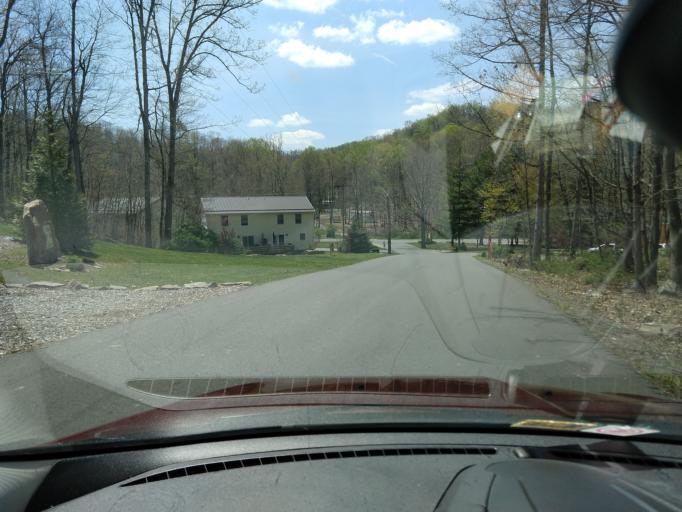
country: US
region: West Virginia
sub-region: Raleigh County
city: Bradley
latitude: 37.8552
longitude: -81.2054
